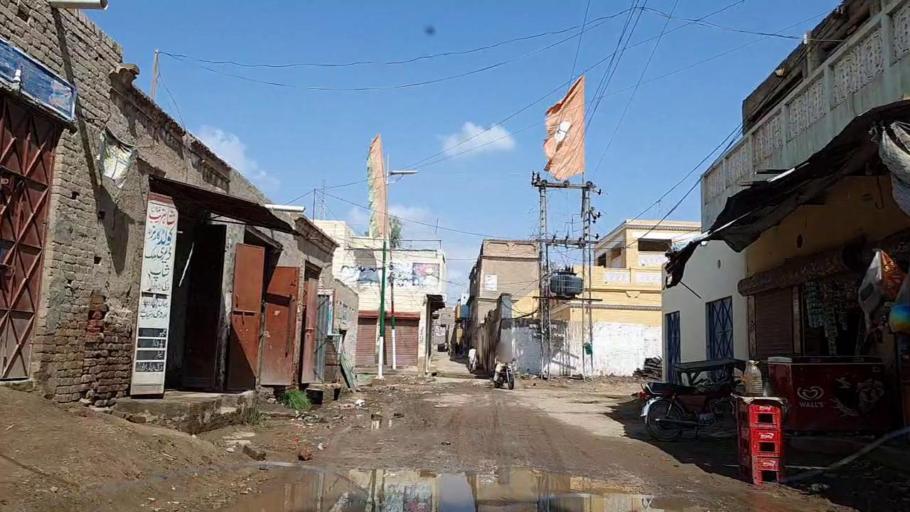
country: PK
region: Sindh
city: Pad Idan
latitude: 26.7748
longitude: 68.2993
